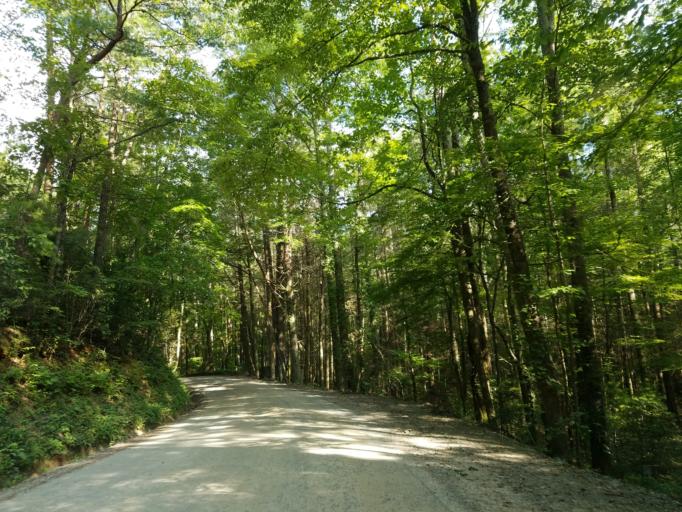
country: US
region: Georgia
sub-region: Fannin County
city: Blue Ridge
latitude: 34.7836
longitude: -84.3407
